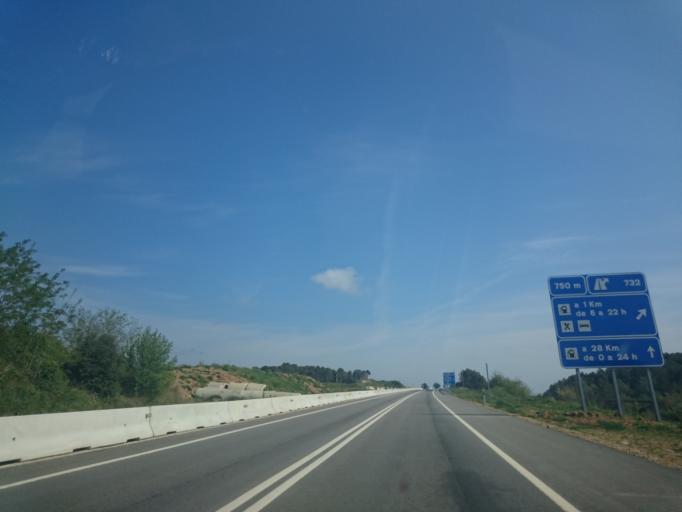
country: ES
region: Catalonia
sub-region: Provincia de Girona
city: Cervia de Ter
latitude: 42.0874
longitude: 2.8902
